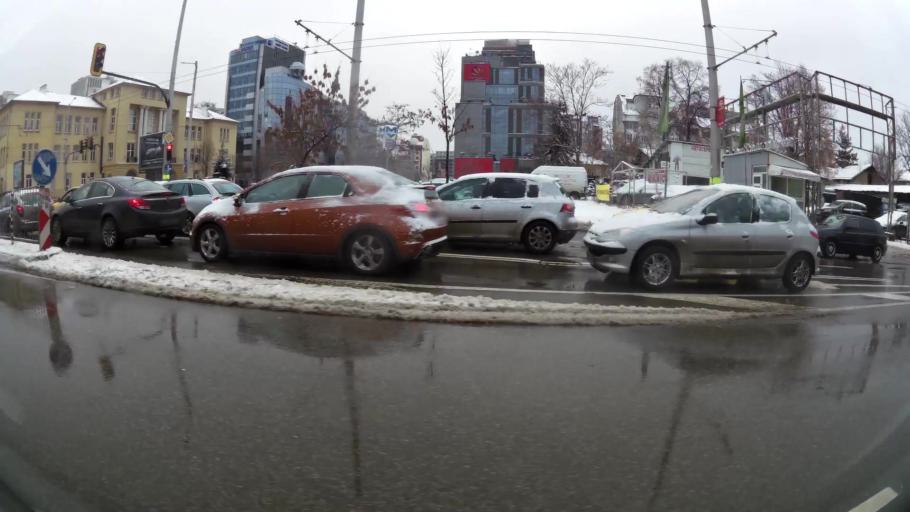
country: BG
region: Sofia-Capital
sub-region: Stolichna Obshtina
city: Sofia
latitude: 42.7004
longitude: 23.3102
